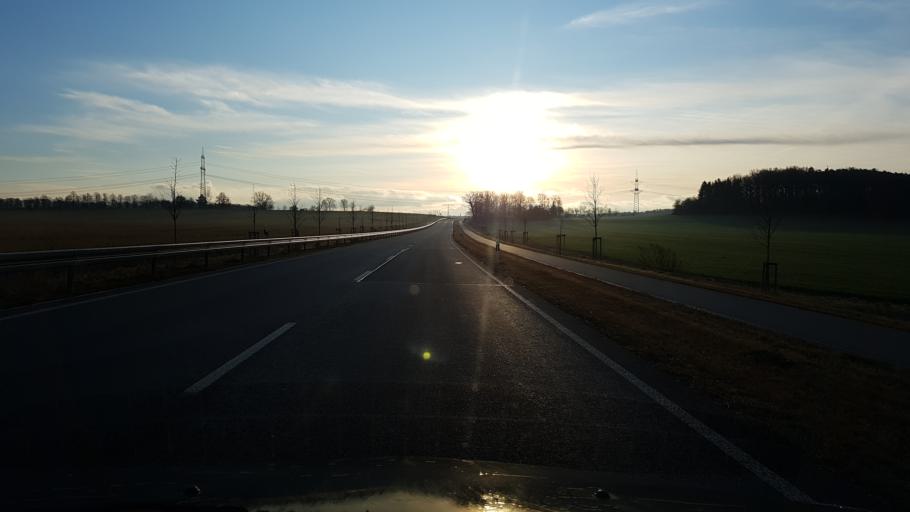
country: DE
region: Saxony
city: Neschwitz
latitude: 51.2461
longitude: 14.3585
